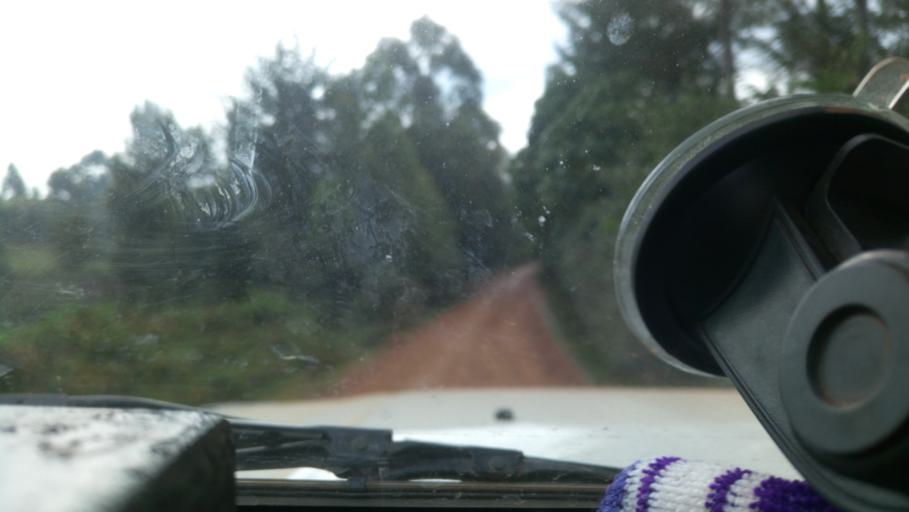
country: KE
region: Kericho
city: Litein
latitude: -0.5881
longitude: 35.2052
